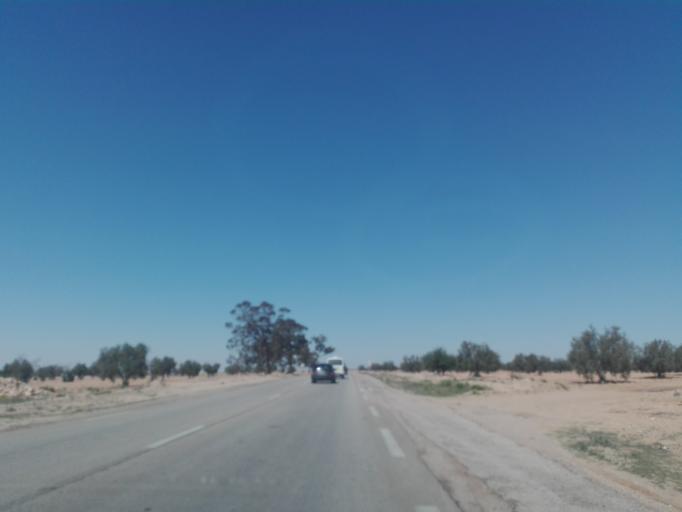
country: TN
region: Safaqis
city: Bi'r `Ali Bin Khalifah
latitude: 34.7587
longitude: 10.3055
